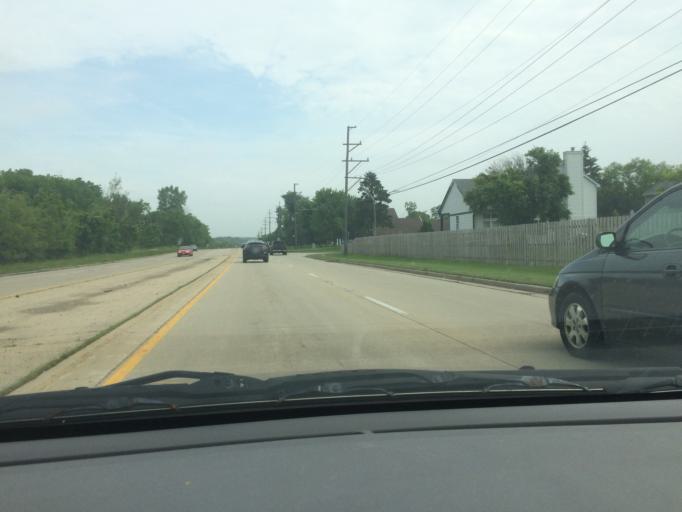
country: US
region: Illinois
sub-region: Cook County
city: Bartlett
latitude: 41.9669
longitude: -88.2065
